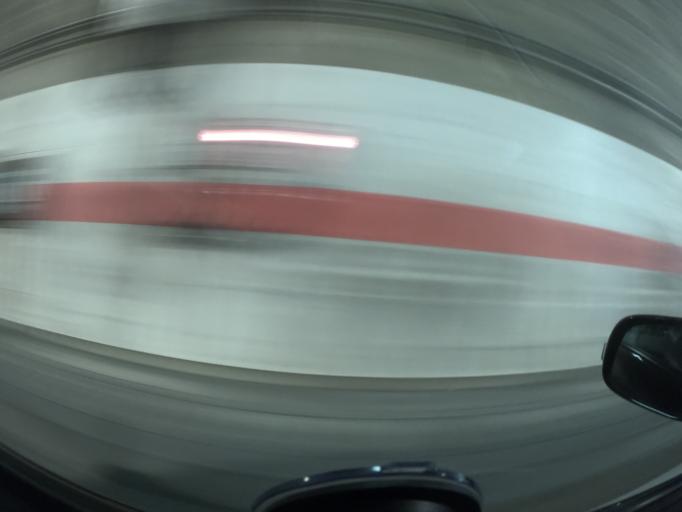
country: JP
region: Shizuoka
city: Shizuoka-shi
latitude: 35.1346
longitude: 138.1444
